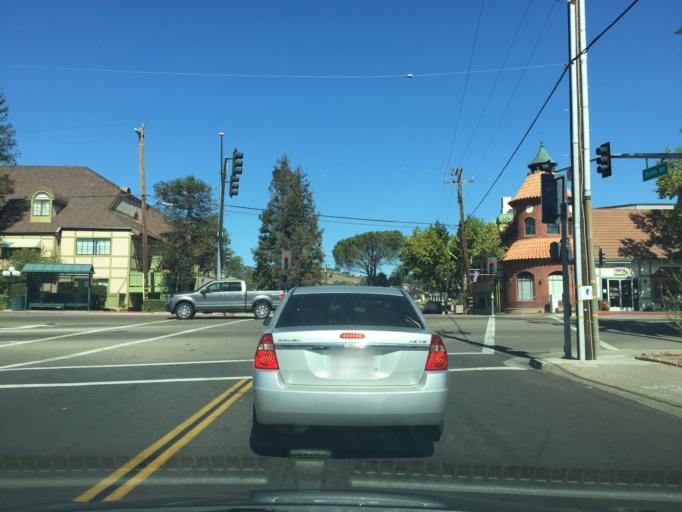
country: US
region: California
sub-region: Santa Barbara County
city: Solvang
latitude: 34.5958
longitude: -120.1453
